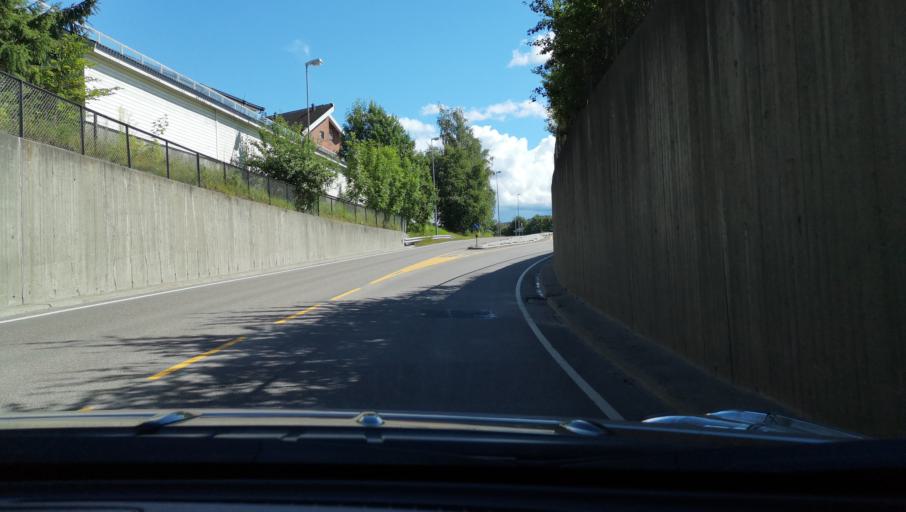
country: NO
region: Akershus
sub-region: As
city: As
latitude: 59.6658
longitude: 10.7938
